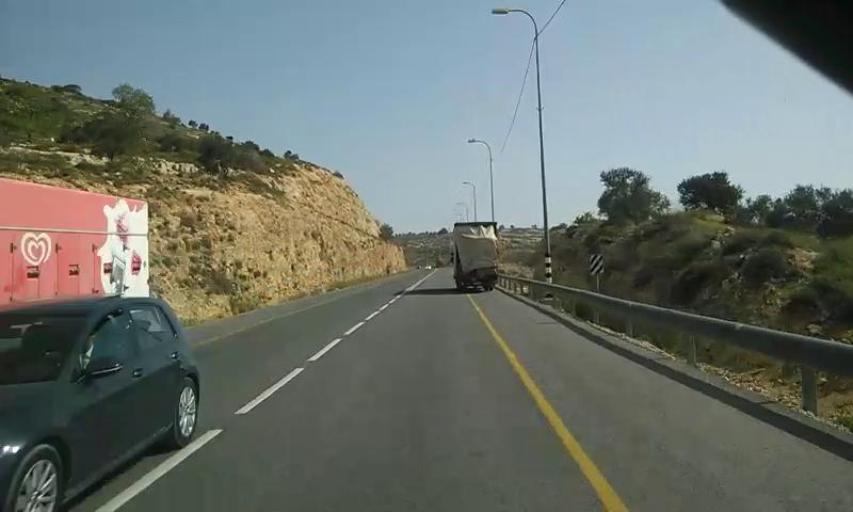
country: PS
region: West Bank
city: Yatma
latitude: 32.1093
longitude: 35.2571
